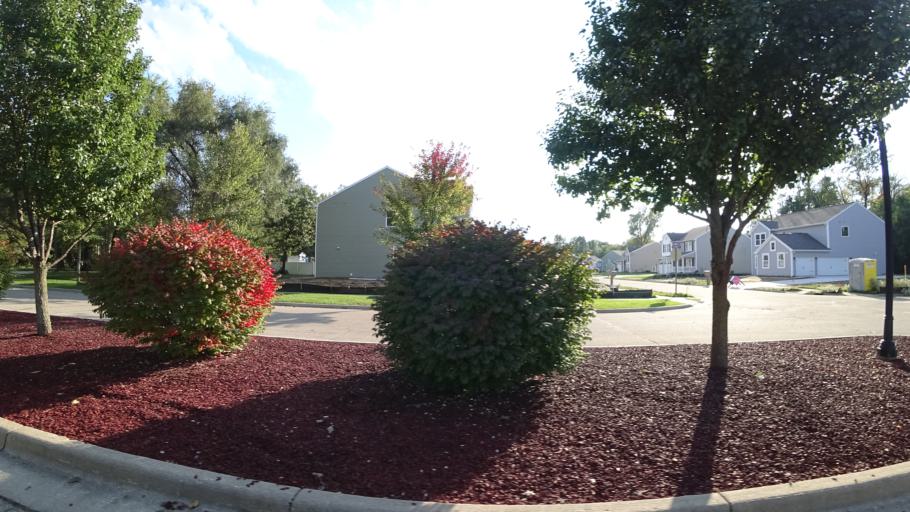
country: US
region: Michigan
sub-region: Saint Joseph County
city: Three Rivers
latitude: 41.9609
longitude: -85.6248
